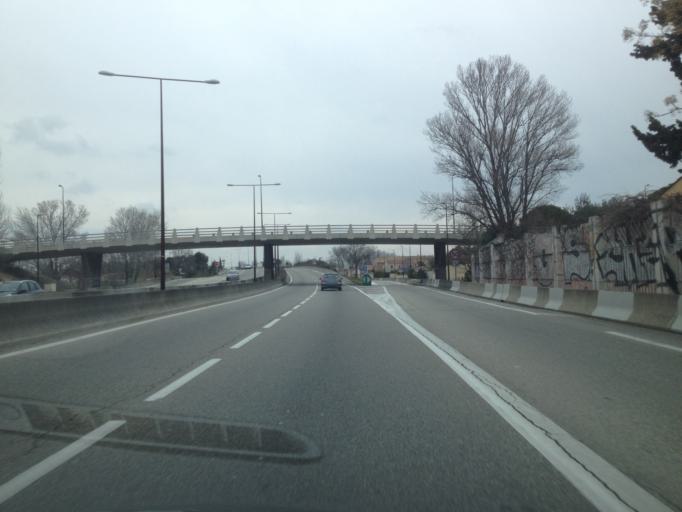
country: FR
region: Provence-Alpes-Cote d'Azur
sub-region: Departement du Vaucluse
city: Le Pontet
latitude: 43.9498
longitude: 4.8409
